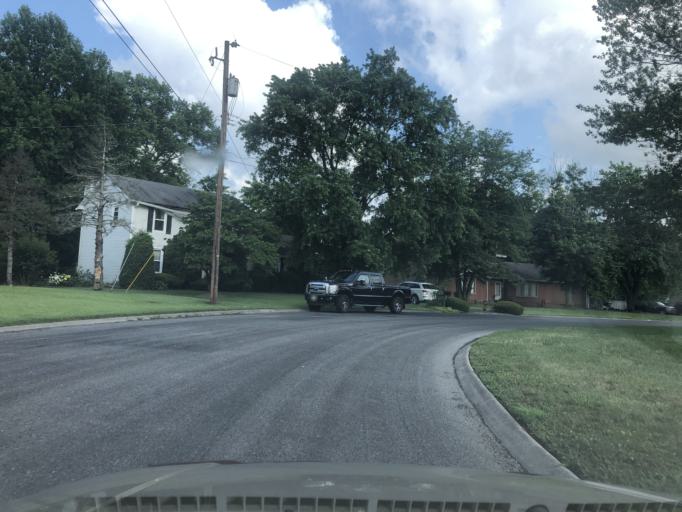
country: US
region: Tennessee
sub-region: Davidson County
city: Lakewood
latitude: 36.2297
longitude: -86.5935
